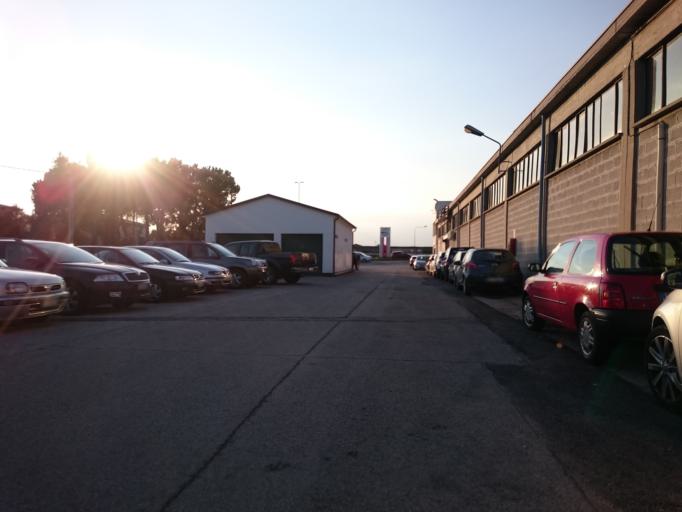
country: IT
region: Veneto
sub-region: Provincia di Padova
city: Terradura
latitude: 45.3352
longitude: 11.8226
